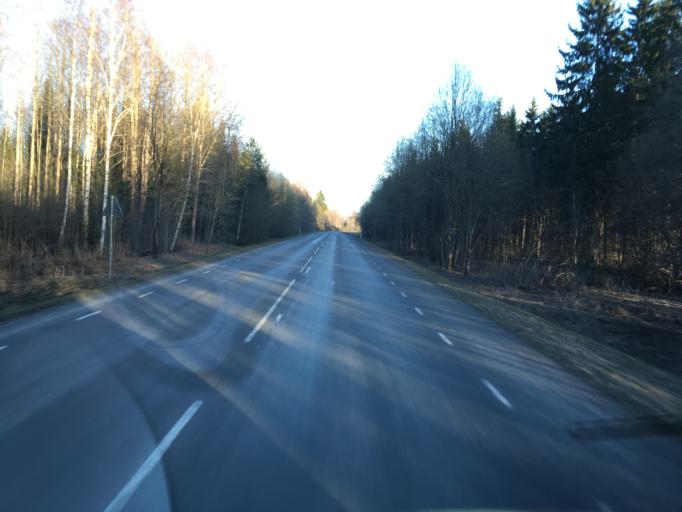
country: EE
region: Raplamaa
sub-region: Kehtna vald
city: Kehtna
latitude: 59.0642
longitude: 24.9292
